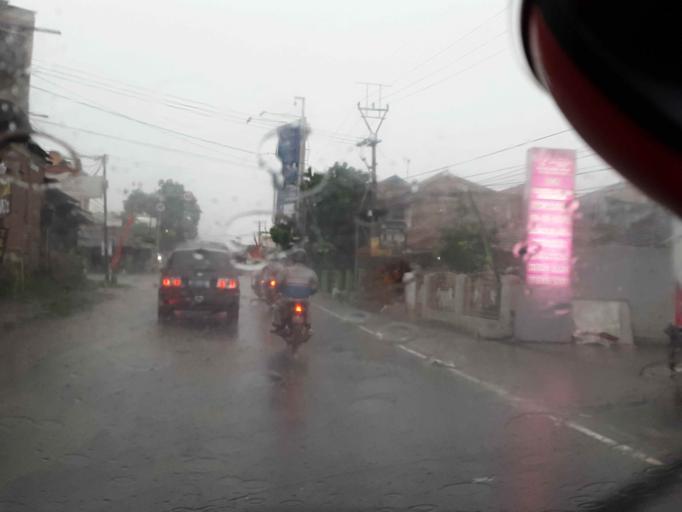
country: ID
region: West Java
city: Cimahi
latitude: -6.8977
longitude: 107.5024
